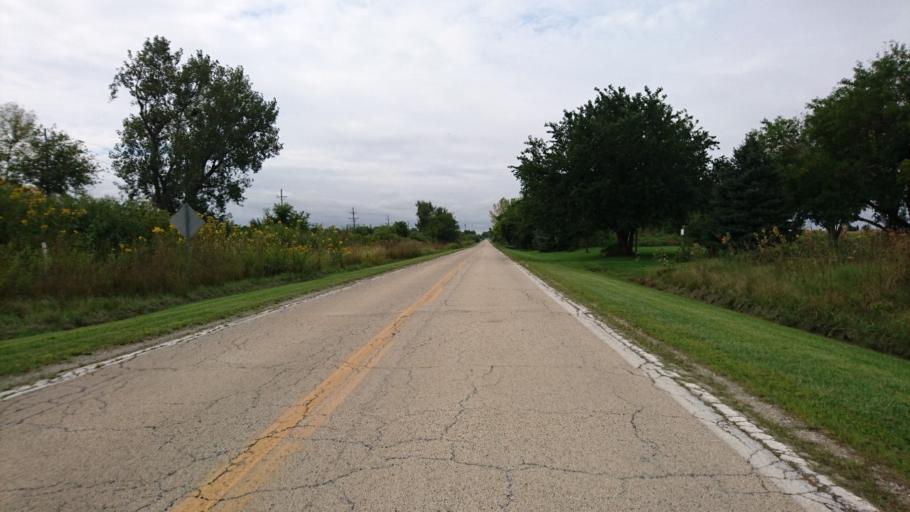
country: US
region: Illinois
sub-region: Livingston County
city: Odell
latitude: 41.0162
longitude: -88.5132
